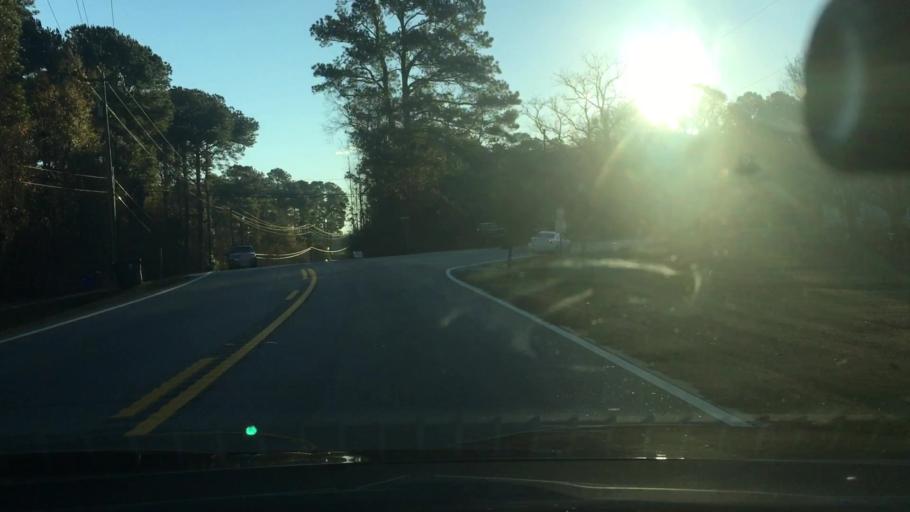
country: US
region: Georgia
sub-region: Fayette County
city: Peachtree City
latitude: 33.3427
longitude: -84.6499
